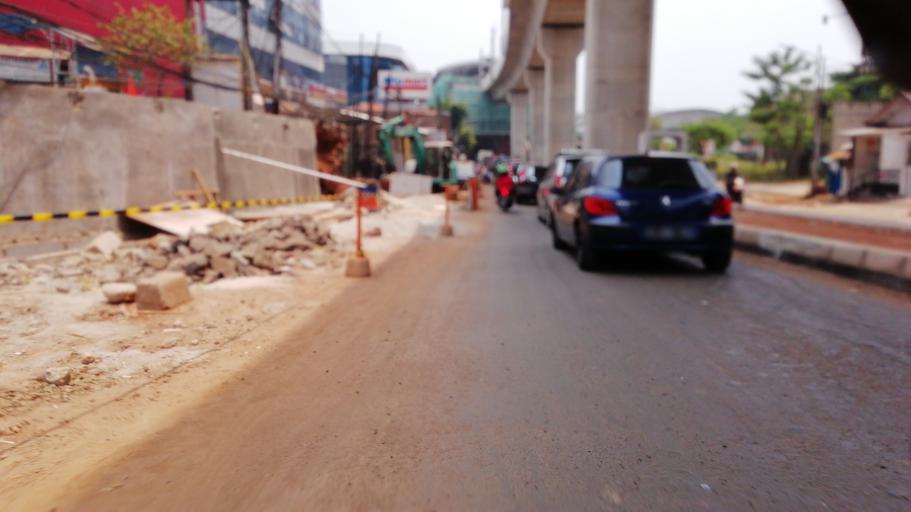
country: ID
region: Banten
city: South Tangerang
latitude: -6.2804
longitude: 106.7965
